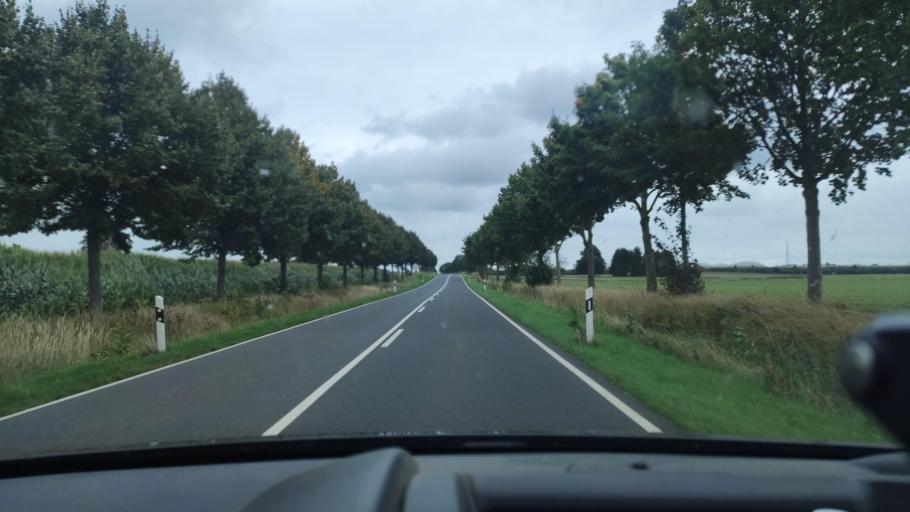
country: DE
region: Mecklenburg-Vorpommern
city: Guestrow
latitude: 53.8282
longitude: 12.1816
